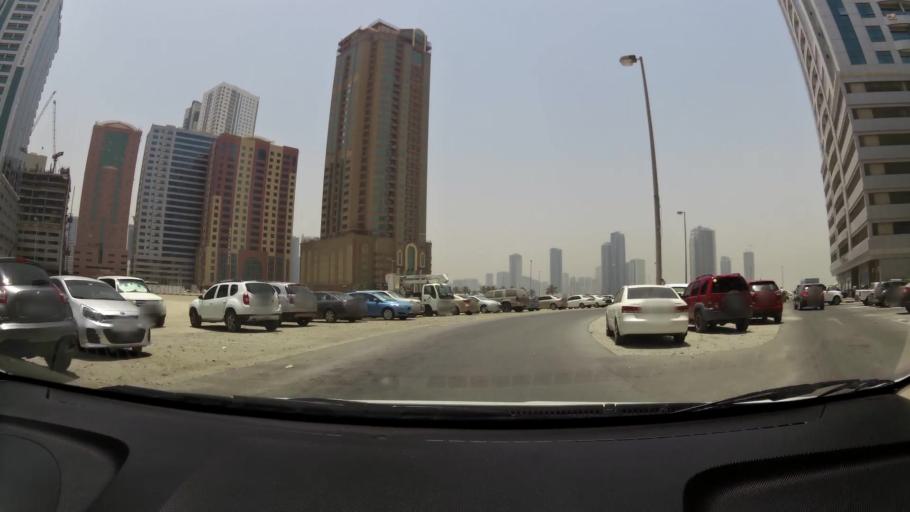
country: AE
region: Ash Shariqah
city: Sharjah
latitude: 25.3297
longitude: 55.3681
